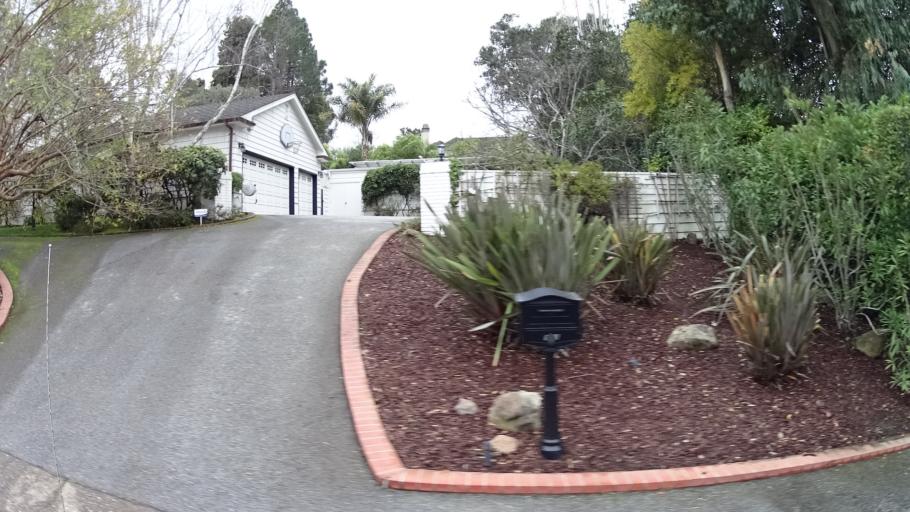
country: US
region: California
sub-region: San Mateo County
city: Burlingame
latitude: 37.5669
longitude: -122.3565
